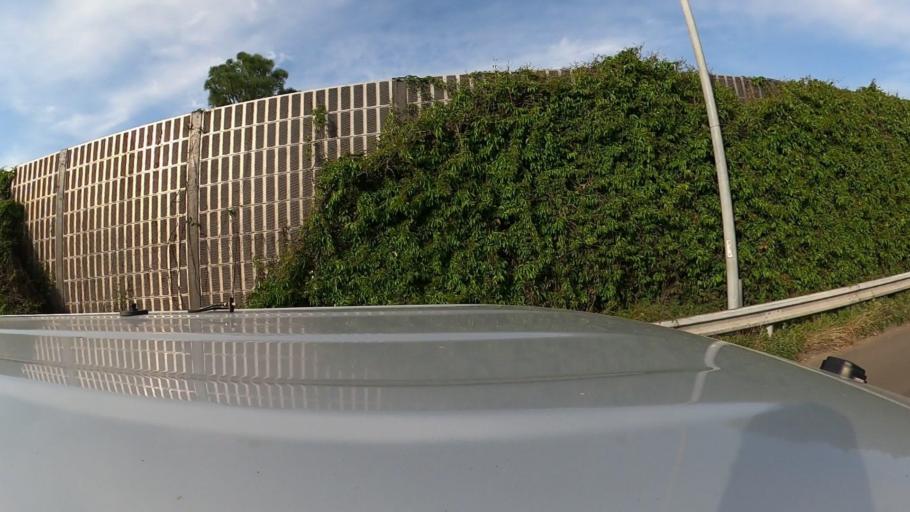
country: JP
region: Saitama
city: Oi
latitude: 35.8015
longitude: 139.5381
